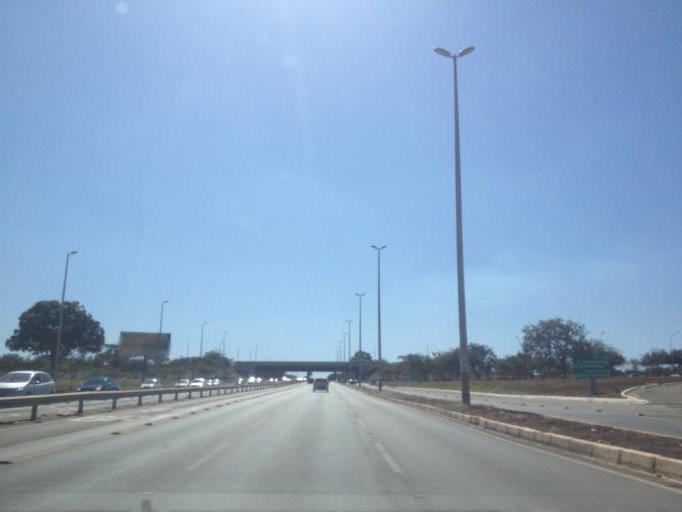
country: BR
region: Federal District
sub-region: Brasilia
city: Brasilia
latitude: -15.8483
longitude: -47.9316
